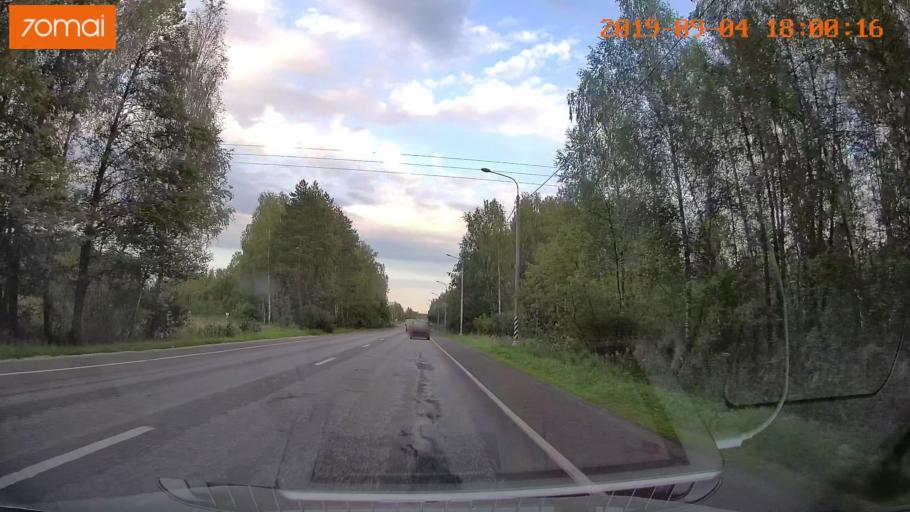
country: RU
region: Moskovskaya
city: Il'inskiy Pogost
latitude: 55.4913
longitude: 38.8589
